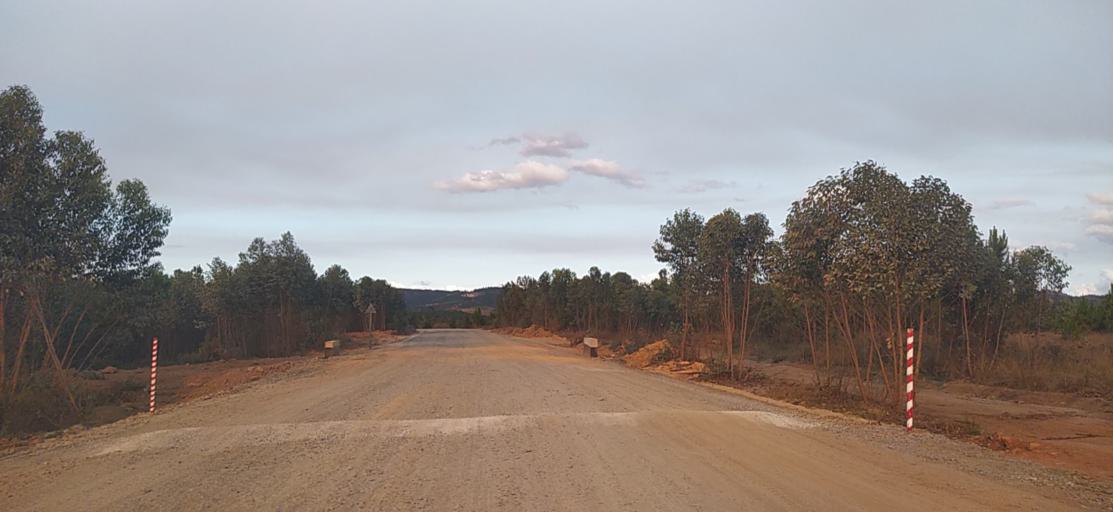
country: MG
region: Analamanga
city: Anjozorobe
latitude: -18.5050
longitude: 48.2659
